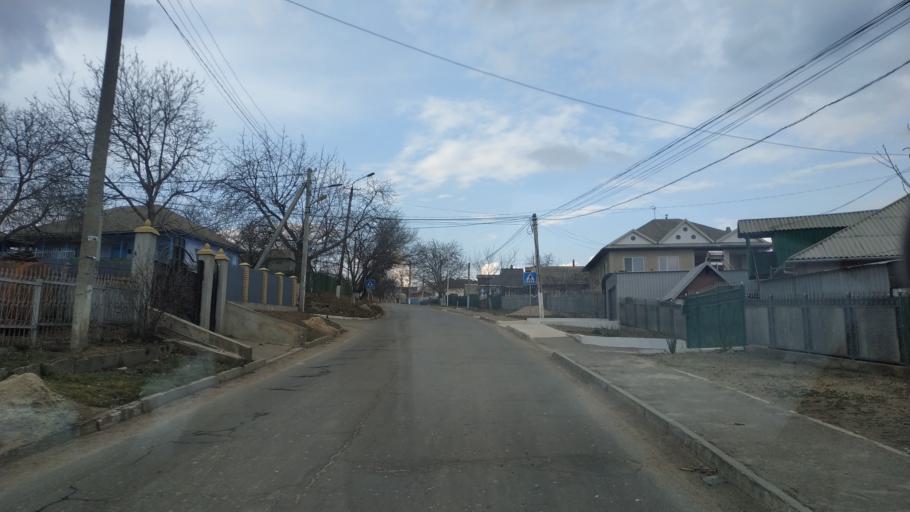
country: MD
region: Anenii Noi
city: Varnita
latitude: 46.8478
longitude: 29.3559
